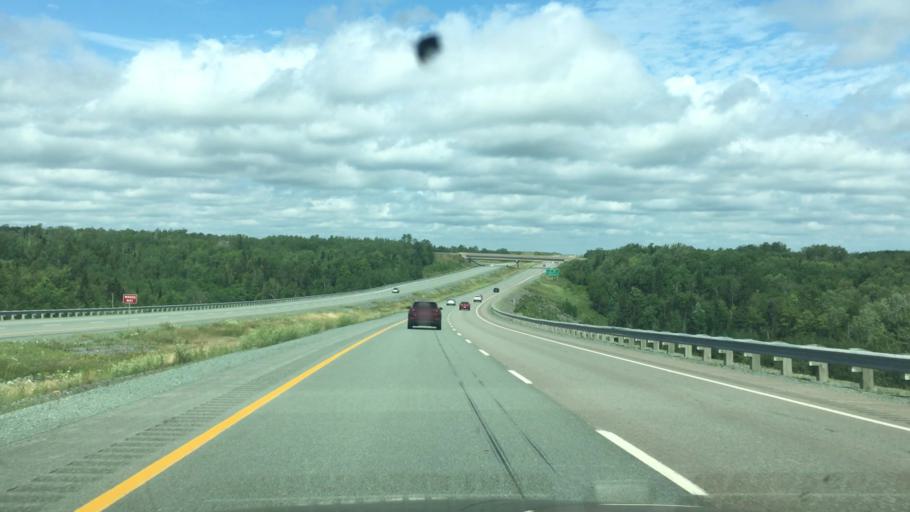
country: CA
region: Nova Scotia
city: Oxford
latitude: 45.6021
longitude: -63.7327
